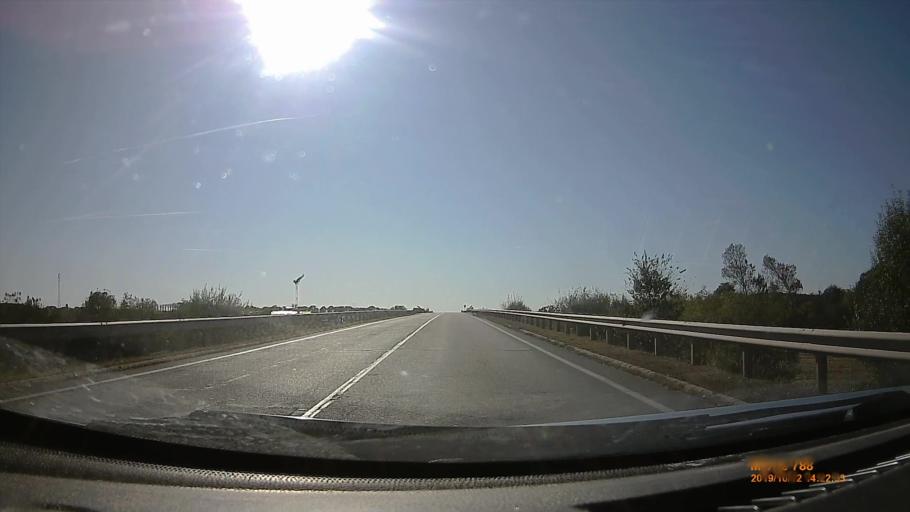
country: HU
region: Hajdu-Bihar
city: Biharkeresztes
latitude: 47.1396
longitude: 21.7084
